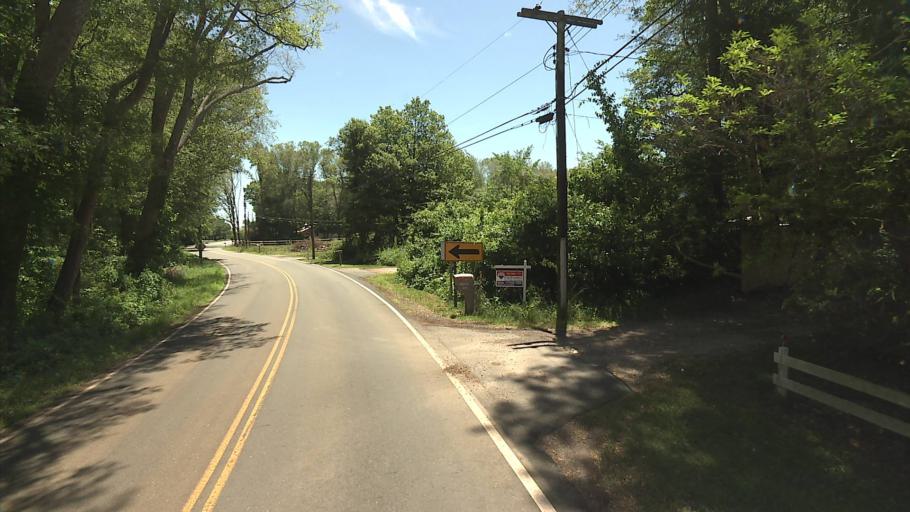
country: US
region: Connecticut
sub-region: New London County
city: Old Mystic
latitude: 41.3765
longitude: -71.9214
